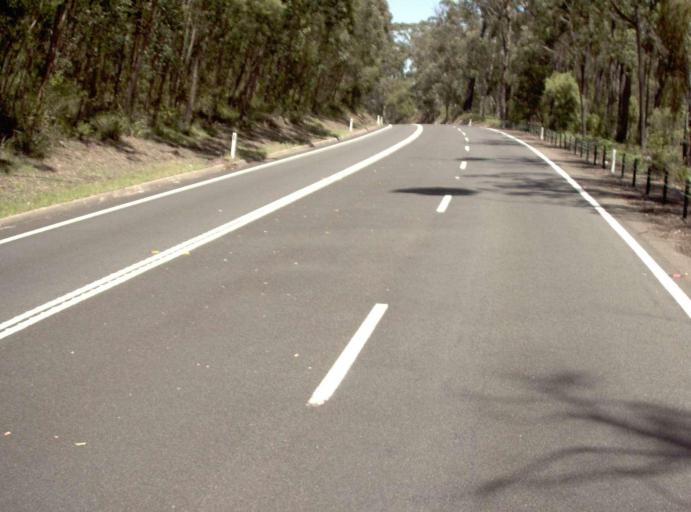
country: AU
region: Victoria
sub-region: East Gippsland
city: Lakes Entrance
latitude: -37.7923
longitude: 148.0498
